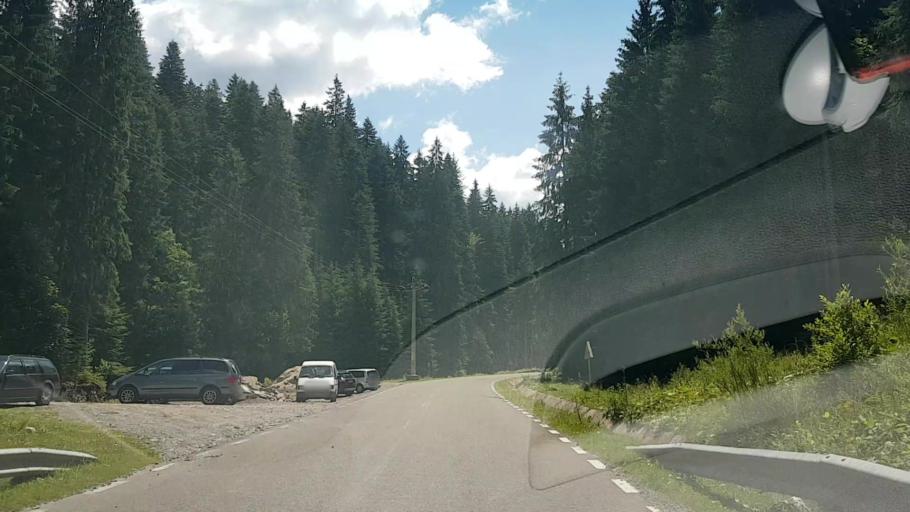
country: RO
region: Suceava
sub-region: Comuna Sadova
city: Sadova
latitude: 47.4788
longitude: 25.4954
